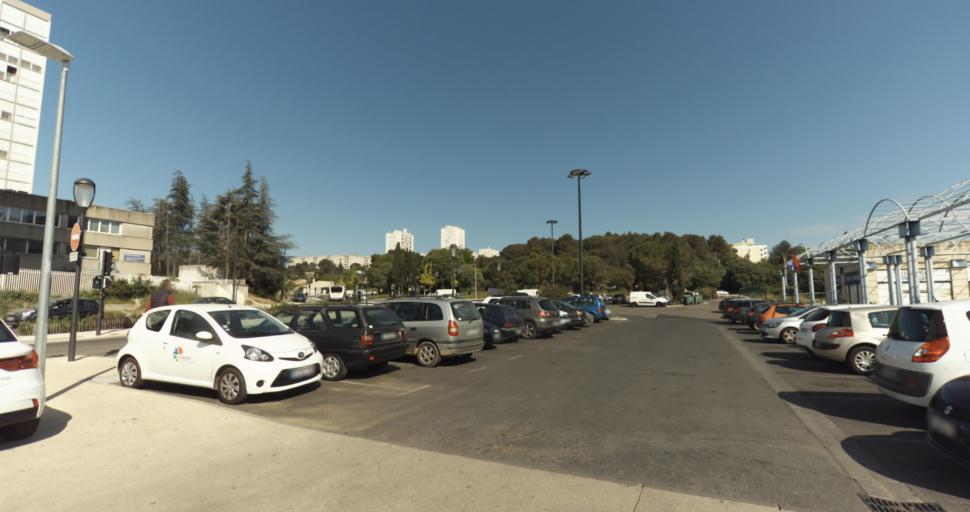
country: FR
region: Languedoc-Roussillon
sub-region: Departement du Gard
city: Nimes
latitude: 43.8258
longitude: 4.3338
